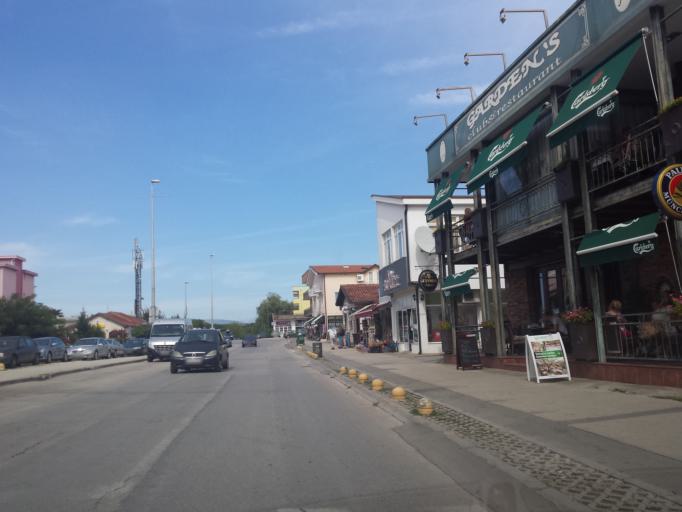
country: BA
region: Federation of Bosnia and Herzegovina
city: Citluk
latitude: 43.1940
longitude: 17.6788
